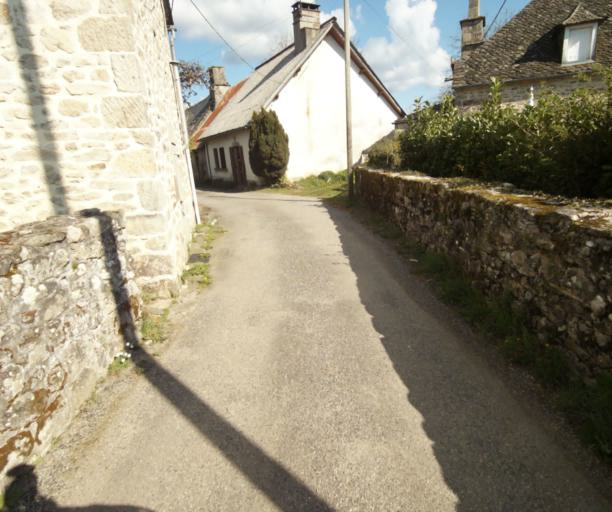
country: FR
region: Limousin
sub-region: Departement de la Correze
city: Laguenne
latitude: 45.2372
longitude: 1.9068
